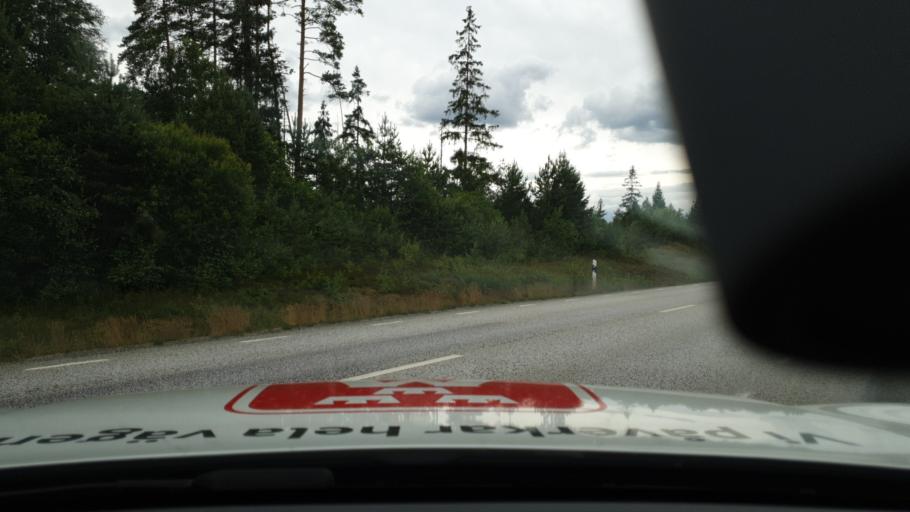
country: SE
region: Joenkoeping
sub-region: Gnosjo Kommun
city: Hillerstorp
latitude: 57.2896
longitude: 13.8362
